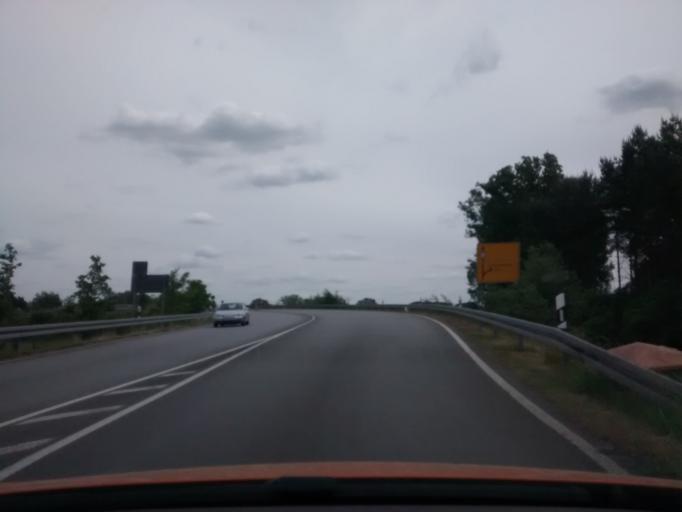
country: DE
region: Brandenburg
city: Trebbin
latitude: 52.2314
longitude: 13.2283
